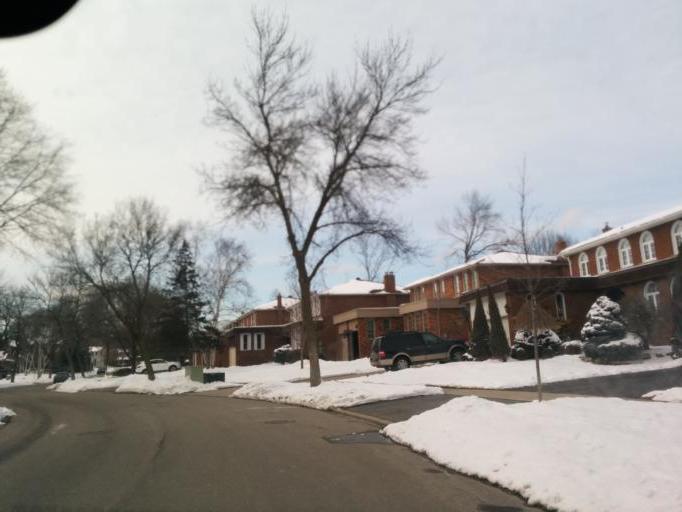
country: CA
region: Ontario
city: Mississauga
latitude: 43.5375
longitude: -79.6594
